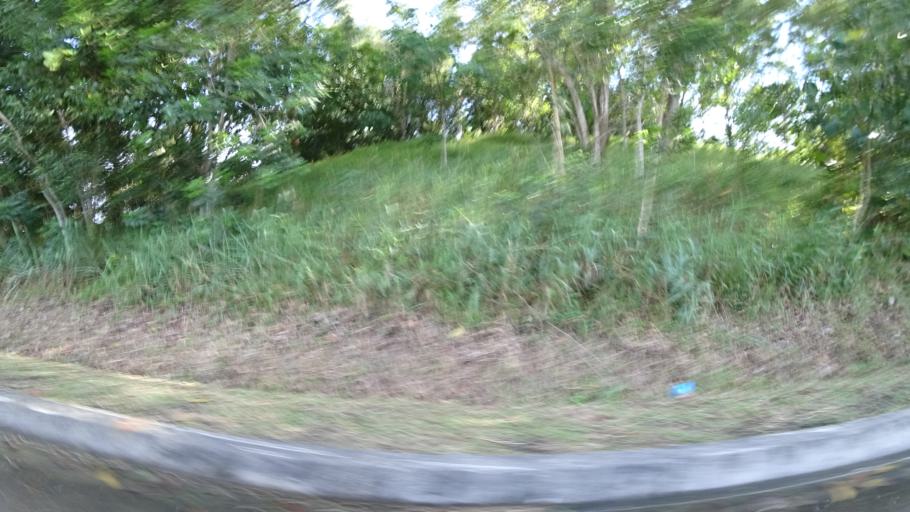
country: BN
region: Brunei and Muara
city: Bandar Seri Begawan
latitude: 4.9782
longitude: 114.9806
